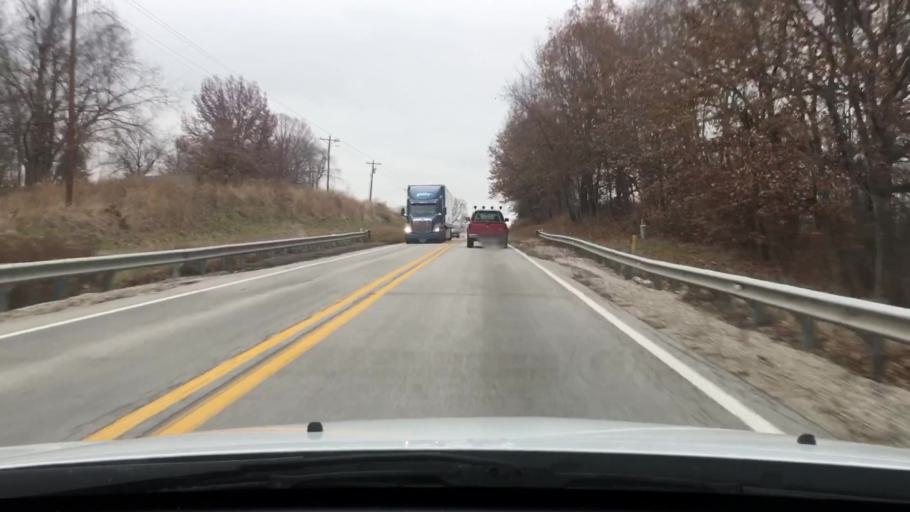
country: US
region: Missouri
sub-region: Pike County
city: Louisiana
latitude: 39.5231
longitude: -90.9426
